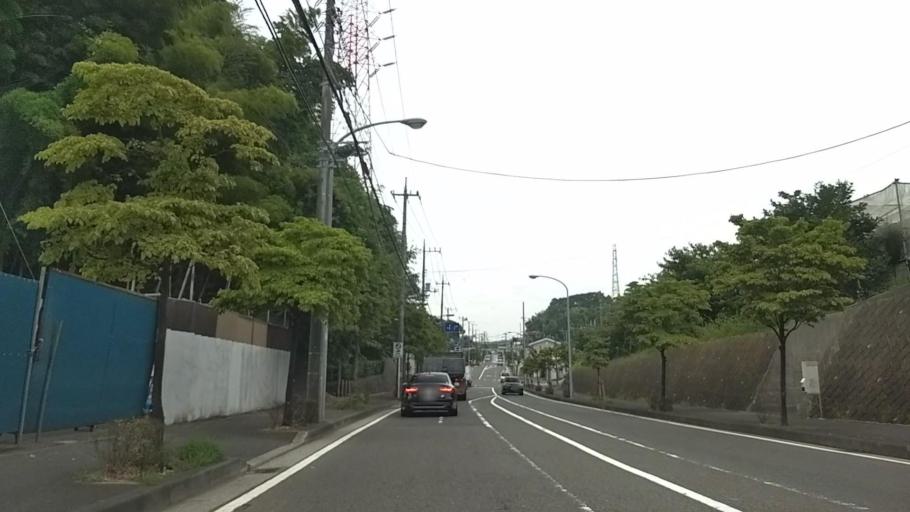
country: JP
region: Kanagawa
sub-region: Kawasaki-shi
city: Kawasaki
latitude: 35.5596
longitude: 139.6084
